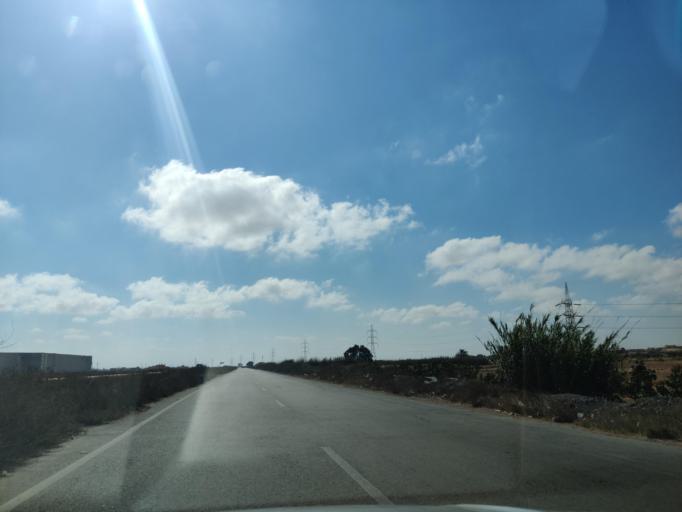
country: EG
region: Muhafazat Matruh
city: Al `Alamayn
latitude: 31.0564
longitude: 28.2525
